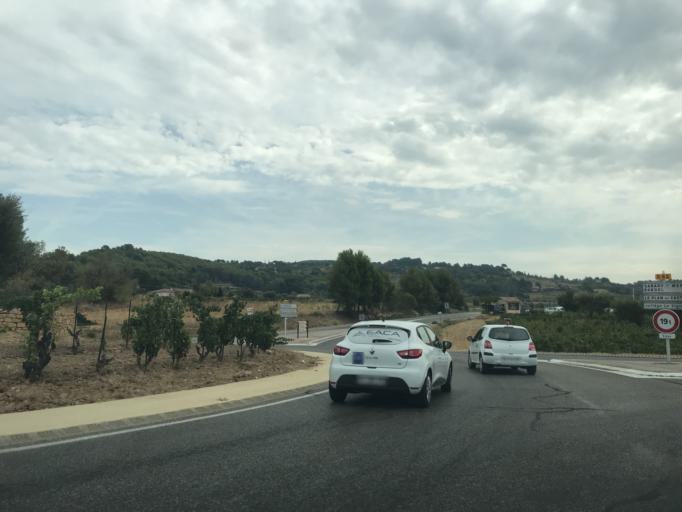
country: FR
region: Provence-Alpes-Cote d'Azur
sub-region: Departement du Var
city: Le Castellet
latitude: 43.1925
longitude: 5.7643
